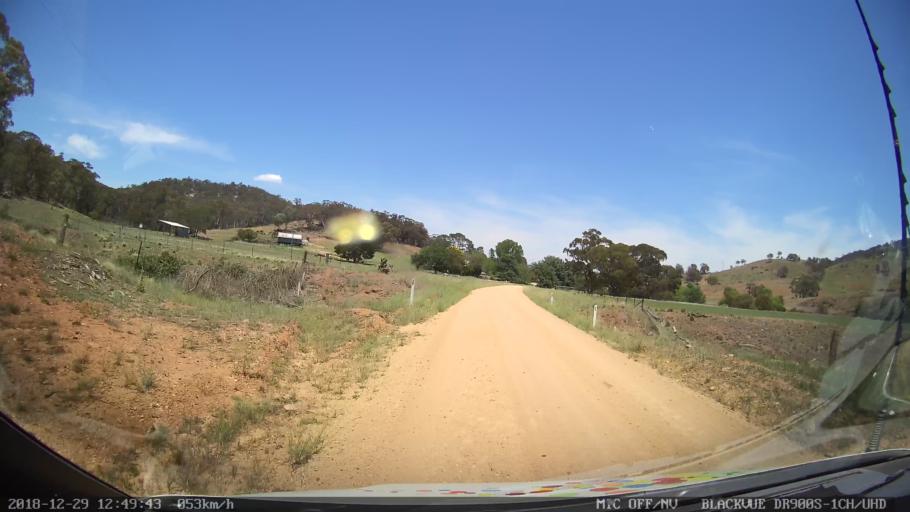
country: AU
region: Australian Capital Territory
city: Macarthur
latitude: -35.6658
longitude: 149.2057
